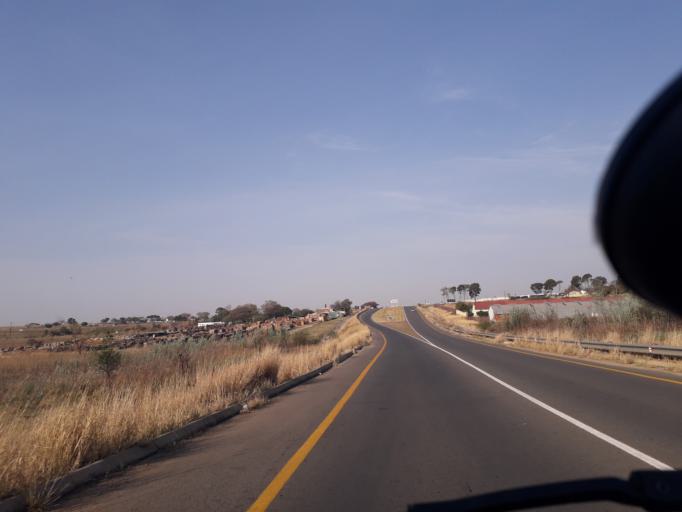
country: ZA
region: Gauteng
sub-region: City of Johannesburg Metropolitan Municipality
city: Diepsloot
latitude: -25.9698
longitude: 27.9168
